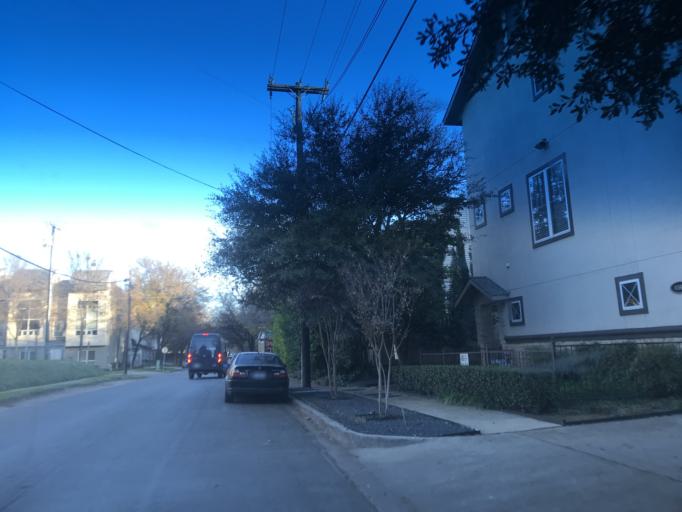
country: US
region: Texas
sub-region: Dallas County
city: Highland Park
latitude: 32.8153
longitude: -96.7954
